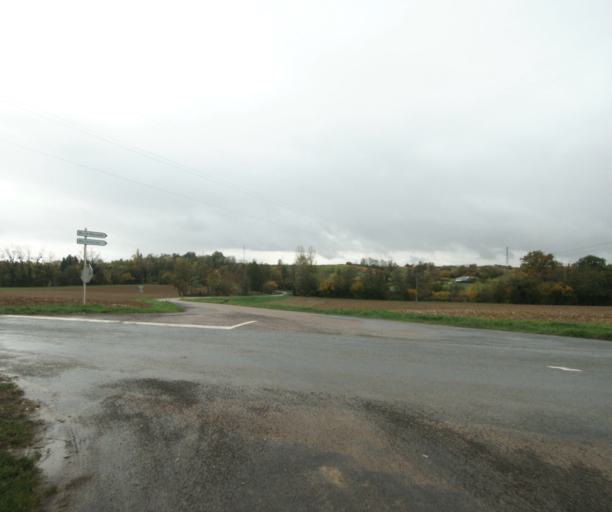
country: FR
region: Rhone-Alpes
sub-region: Departement de l'Ain
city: Pont-de-Vaux
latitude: 46.4765
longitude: 4.8795
